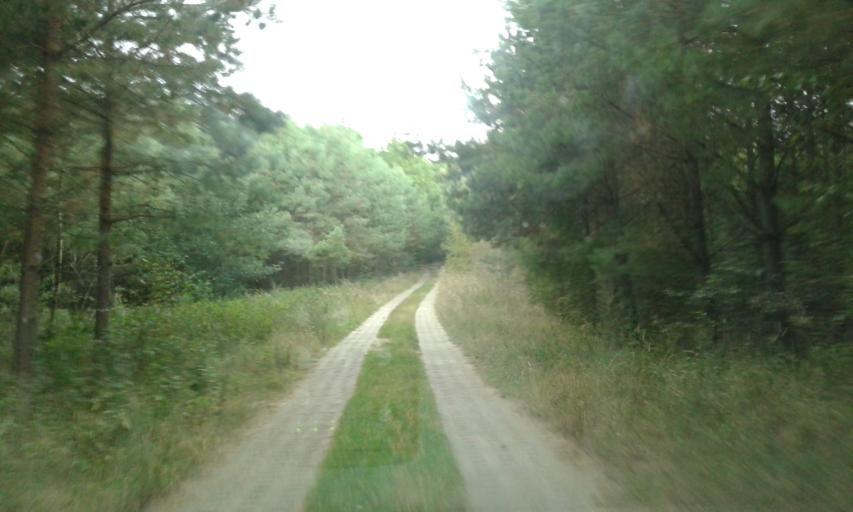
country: PL
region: West Pomeranian Voivodeship
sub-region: Powiat stargardzki
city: Dolice
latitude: 53.1787
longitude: 15.1629
